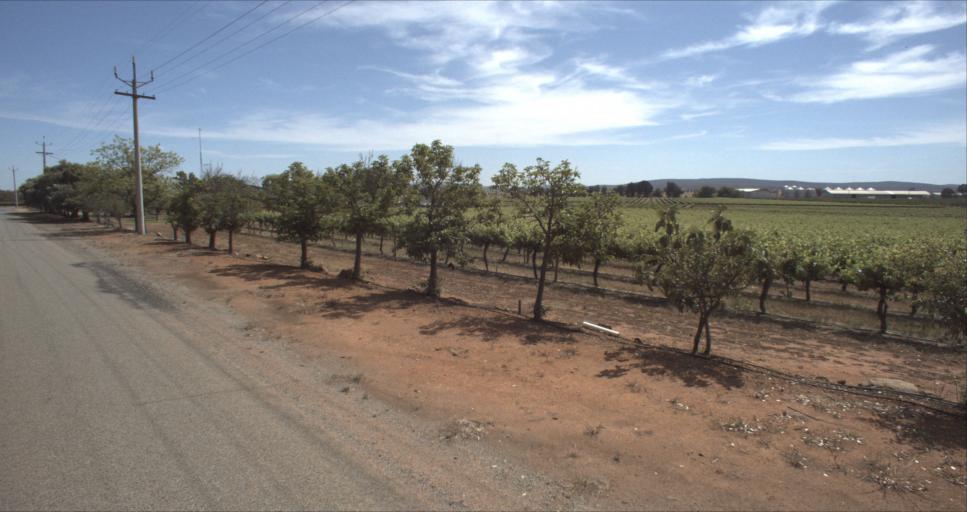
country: AU
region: New South Wales
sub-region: Leeton
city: Leeton
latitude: -34.5627
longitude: 146.4609
